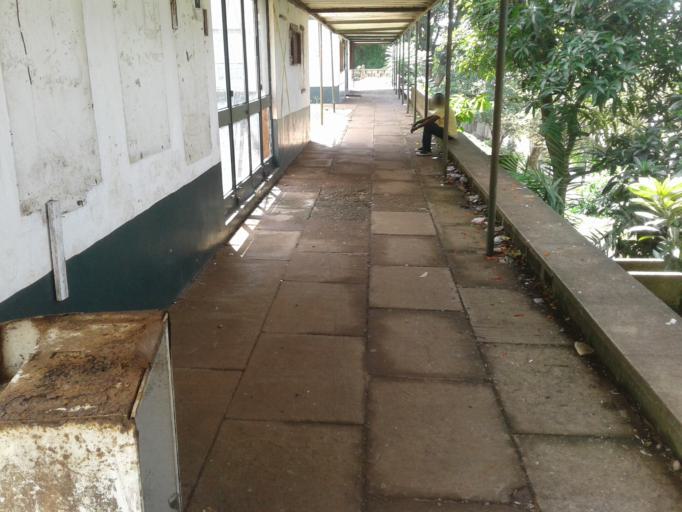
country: SL
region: Western Area
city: Freetown
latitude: 8.4782
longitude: -13.2208
